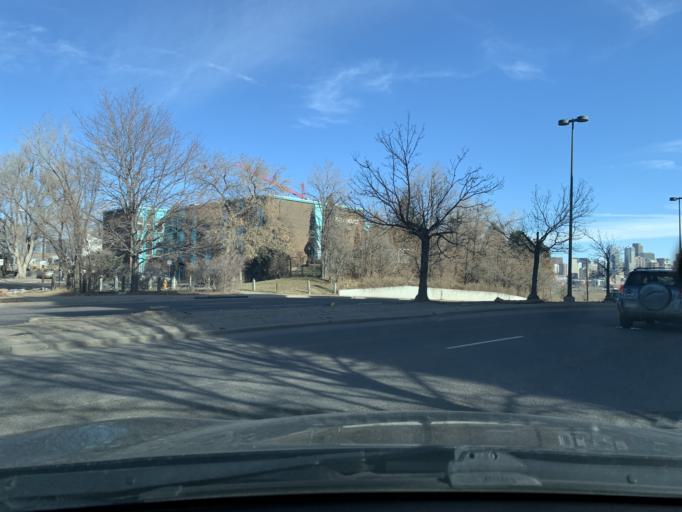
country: US
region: Colorado
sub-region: Jefferson County
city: Edgewater
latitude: 39.7403
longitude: -105.0285
